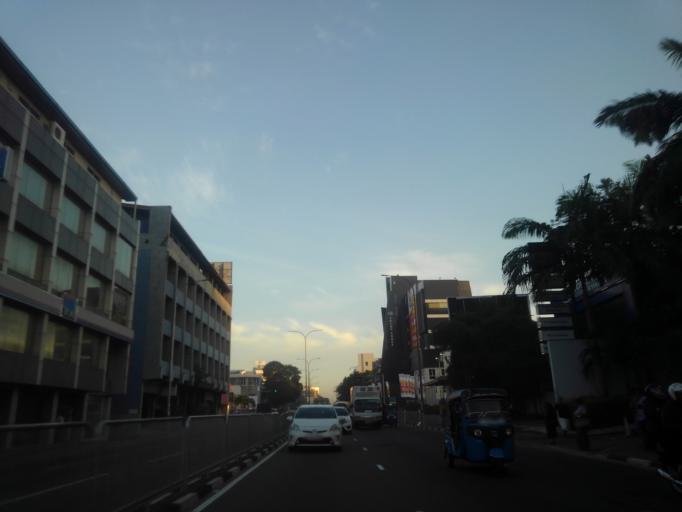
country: LK
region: Western
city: Kolonnawa
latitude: 6.9104
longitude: 79.8775
